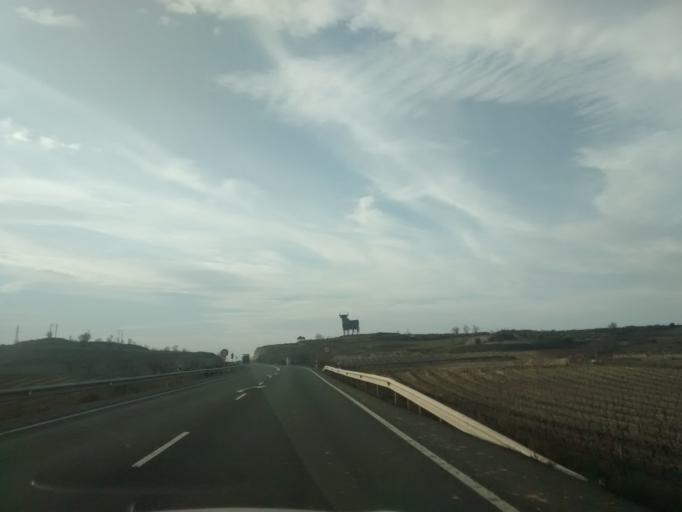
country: ES
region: La Rioja
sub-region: Provincia de La Rioja
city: San Asensio
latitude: 42.5103
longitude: -2.7186
